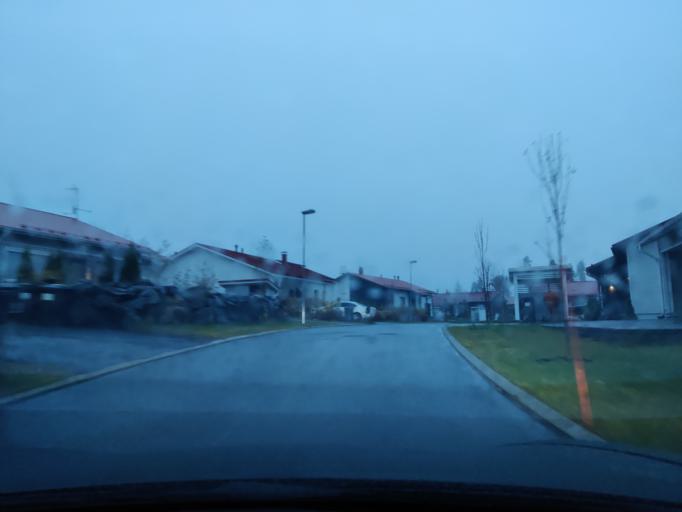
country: FI
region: Northern Savo
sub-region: Kuopio
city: Kuopio
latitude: 62.8265
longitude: 27.7228
